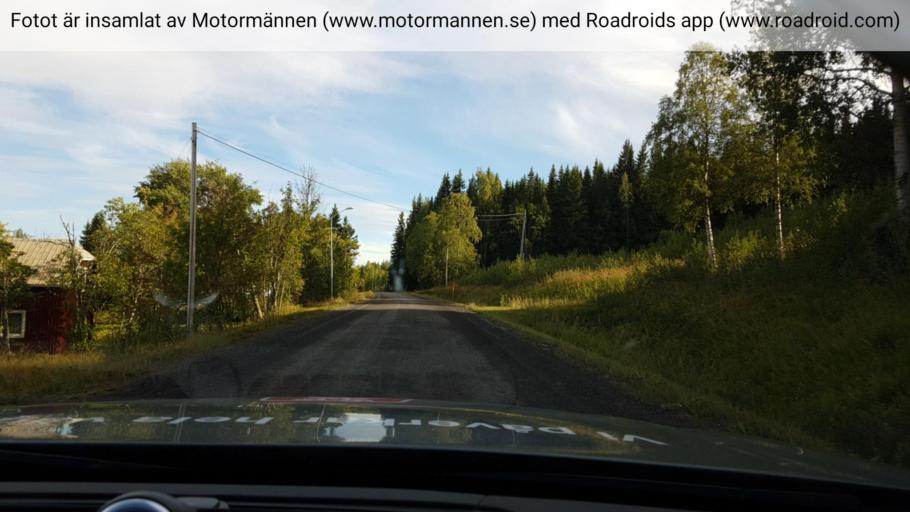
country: SE
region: Jaemtland
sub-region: Stroemsunds Kommun
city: Stroemsund
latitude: 64.1103
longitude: 15.8153
